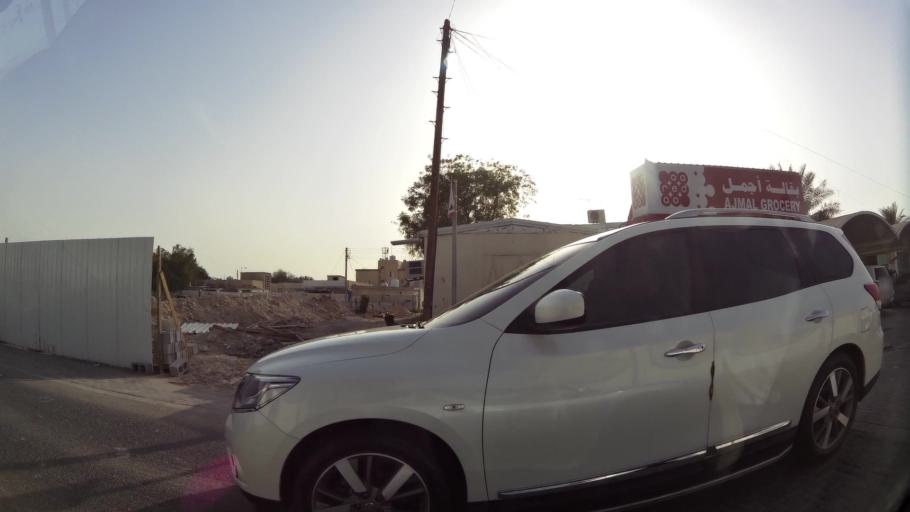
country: QA
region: Baladiyat ar Rayyan
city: Ar Rayyan
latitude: 25.2371
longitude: 51.4430
